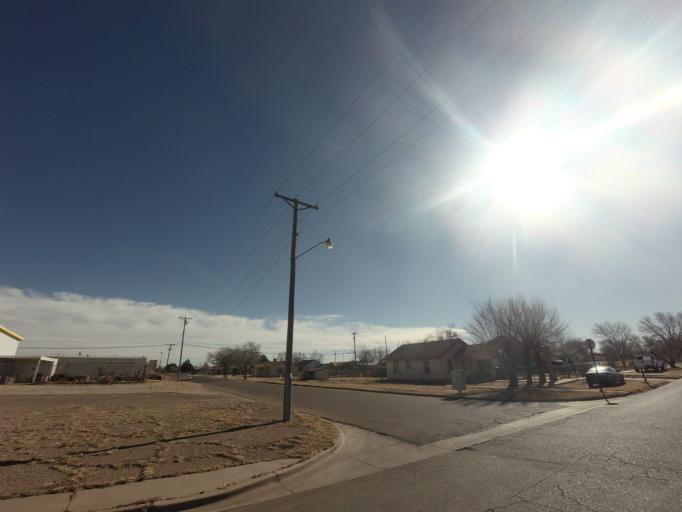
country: US
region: New Mexico
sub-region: Curry County
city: Clovis
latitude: 34.4040
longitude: -103.2192
